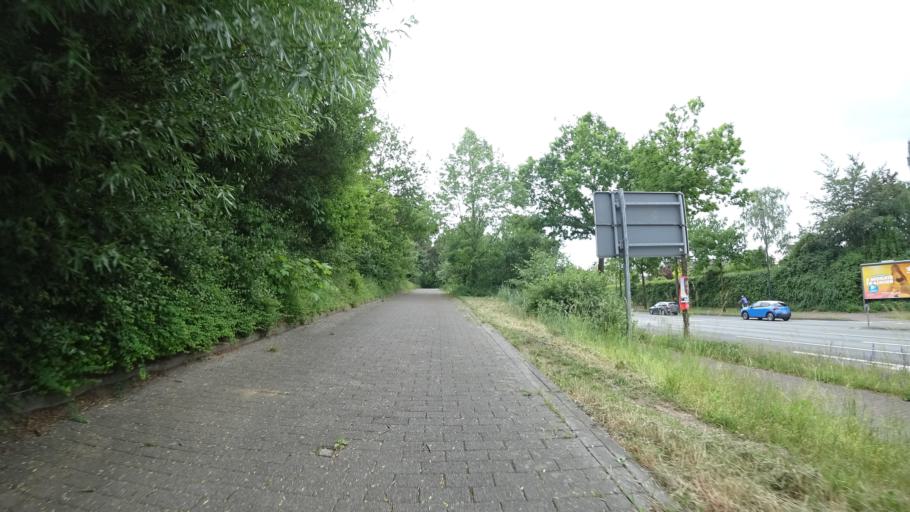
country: DE
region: North Rhine-Westphalia
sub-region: Regierungsbezirk Detmold
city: Guetersloh
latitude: 51.9119
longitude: 8.4071
